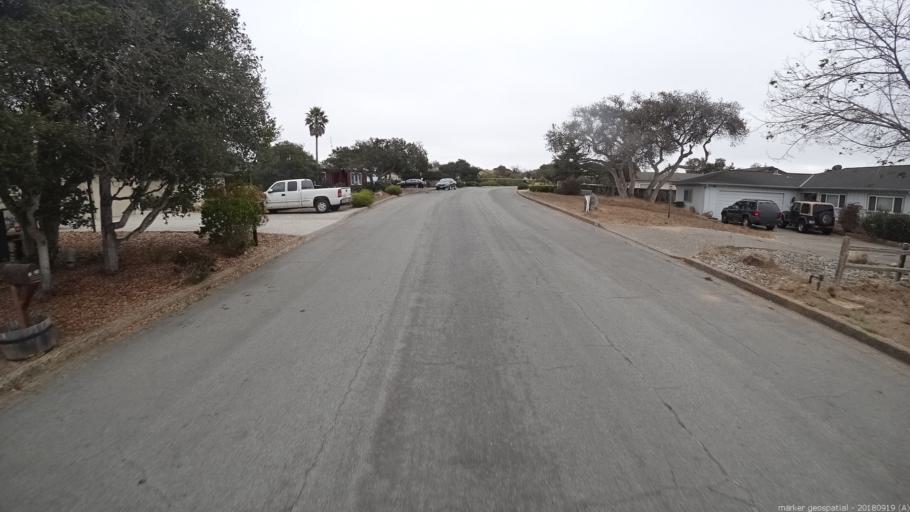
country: US
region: California
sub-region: Monterey County
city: Prunedale
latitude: 36.7814
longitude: -121.7099
